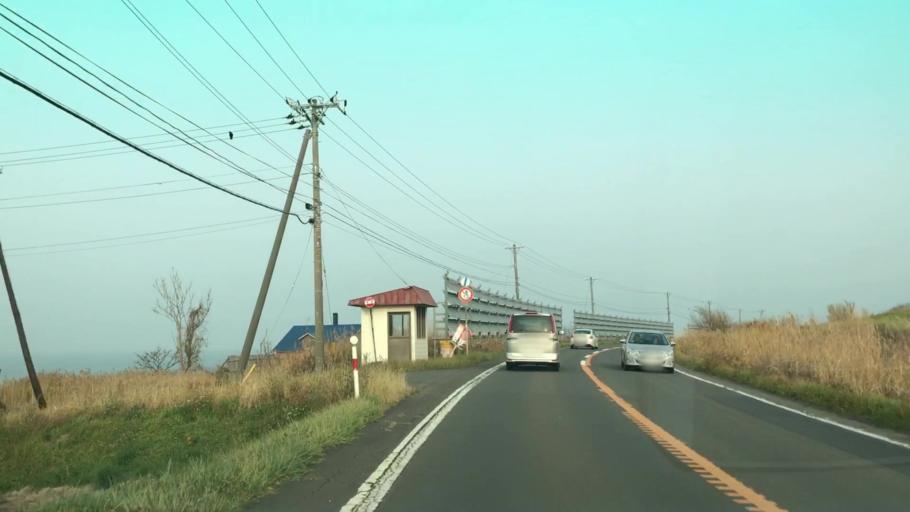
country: JP
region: Hokkaido
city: Ishikari
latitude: 43.3653
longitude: 141.4280
